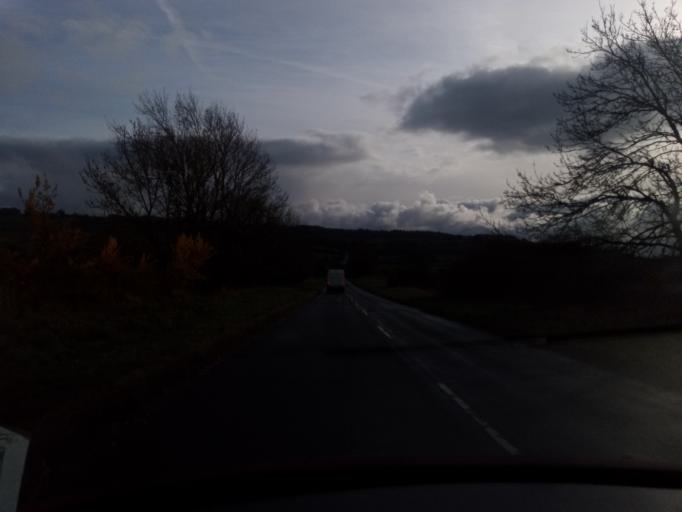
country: GB
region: England
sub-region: Northumberland
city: Wall
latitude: 55.0332
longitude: -2.1320
